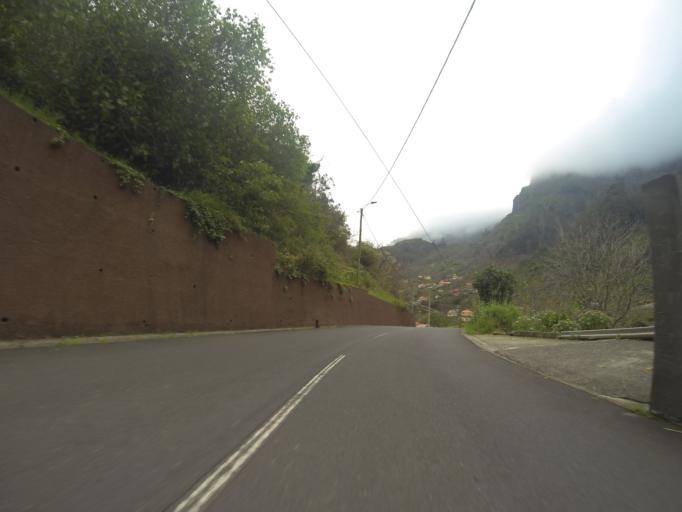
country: PT
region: Madeira
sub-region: Camara de Lobos
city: Curral das Freiras
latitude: 32.7323
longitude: -16.9683
